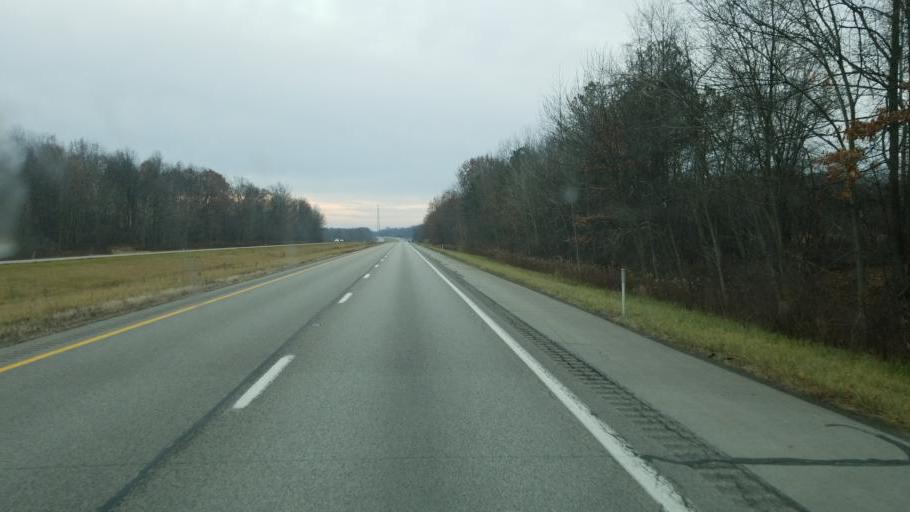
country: US
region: Pennsylvania
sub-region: Crawford County
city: Cochranton
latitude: 41.4808
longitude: -80.1671
